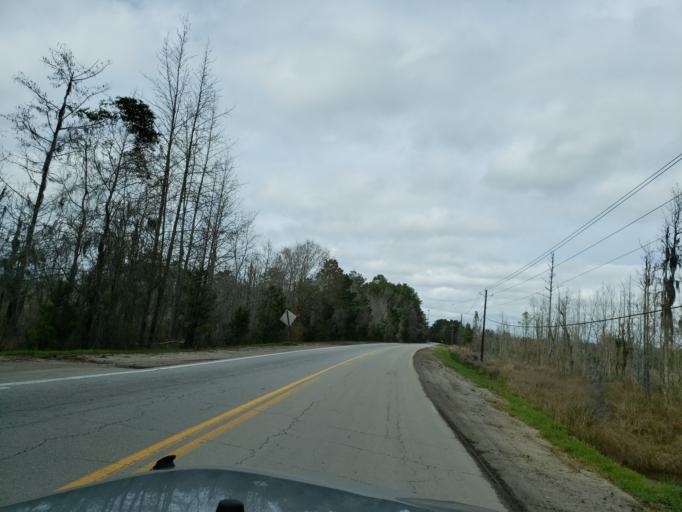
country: US
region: Georgia
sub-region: Chatham County
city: Georgetown
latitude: 32.0311
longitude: -81.2718
